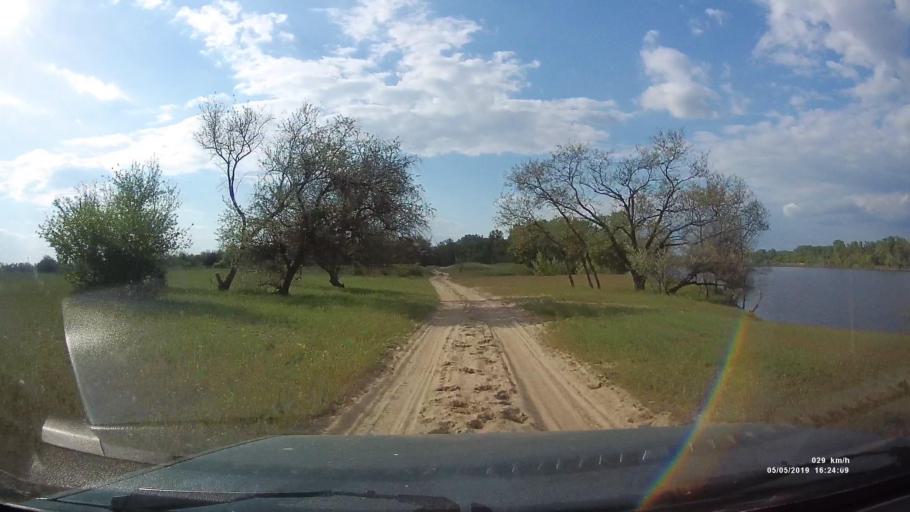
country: RU
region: Rostov
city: Konstantinovsk
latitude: 47.7584
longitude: 41.0273
